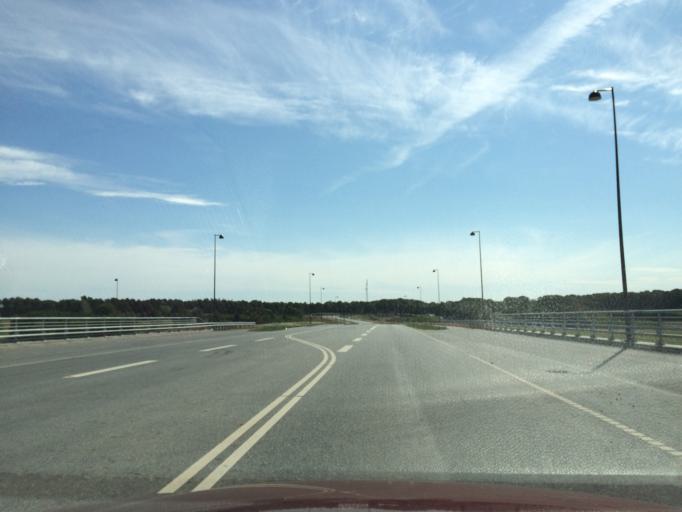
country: DK
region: Central Jutland
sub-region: Silkeborg Kommune
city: Silkeborg
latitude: 56.2013
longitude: 9.5510
